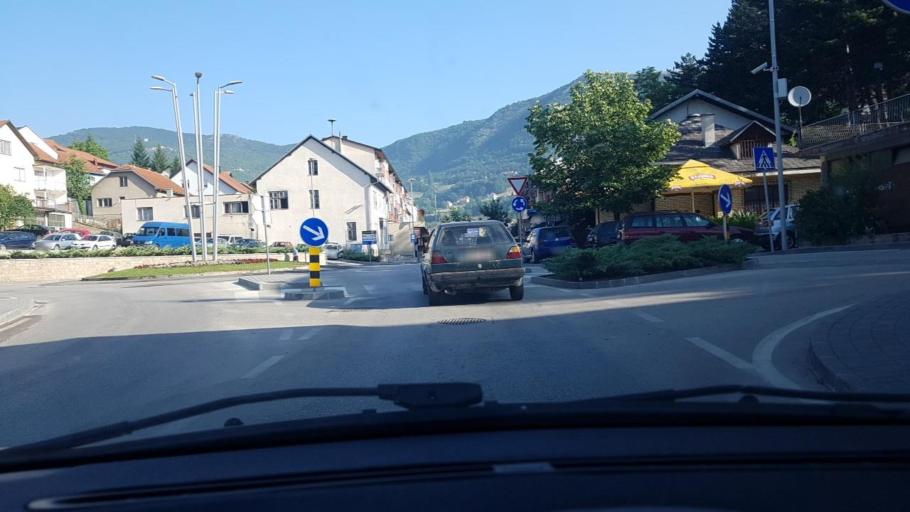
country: BA
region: Federation of Bosnia and Herzegovina
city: Prozor
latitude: 43.8228
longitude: 17.6080
